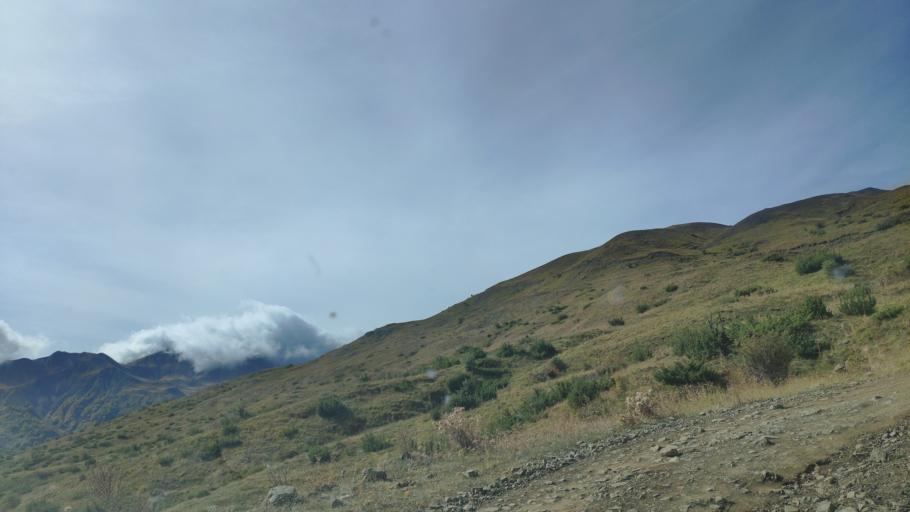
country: AL
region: Korce
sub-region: Rrethi i Kolonjes
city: Erseke
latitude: 40.3799
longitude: 20.8280
